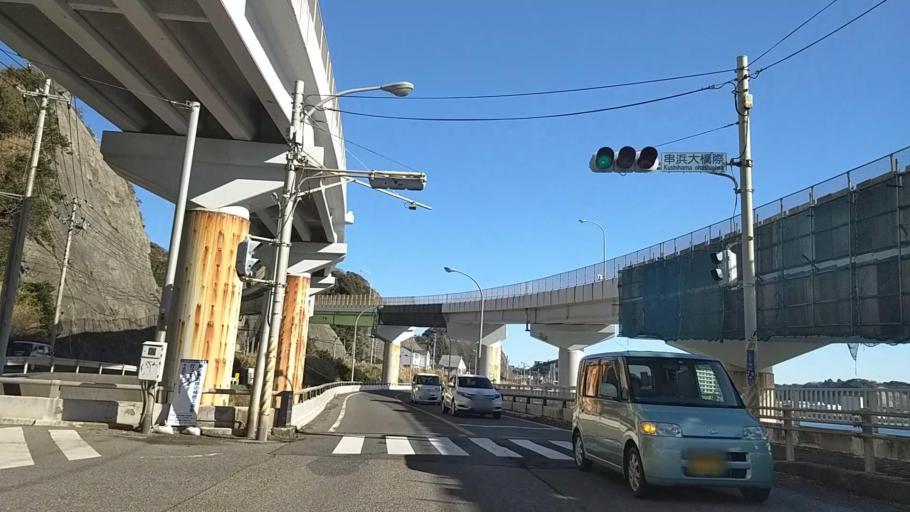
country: JP
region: Chiba
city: Katsuura
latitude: 35.1514
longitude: 140.3026
